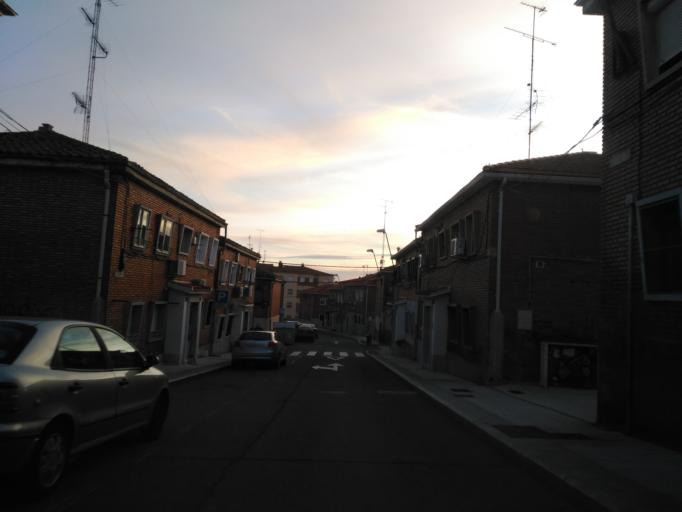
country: ES
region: Castille and Leon
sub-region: Provincia de Salamanca
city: Salamanca
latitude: 40.9748
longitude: -5.6755
